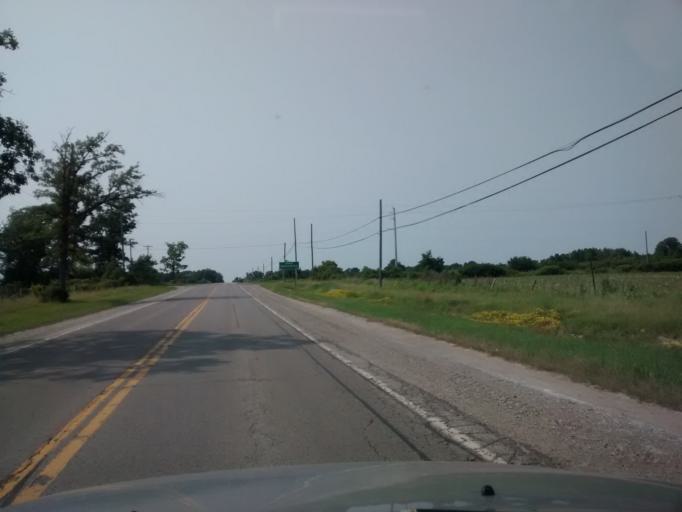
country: CA
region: Ontario
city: Ancaster
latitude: 42.9660
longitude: -79.8656
